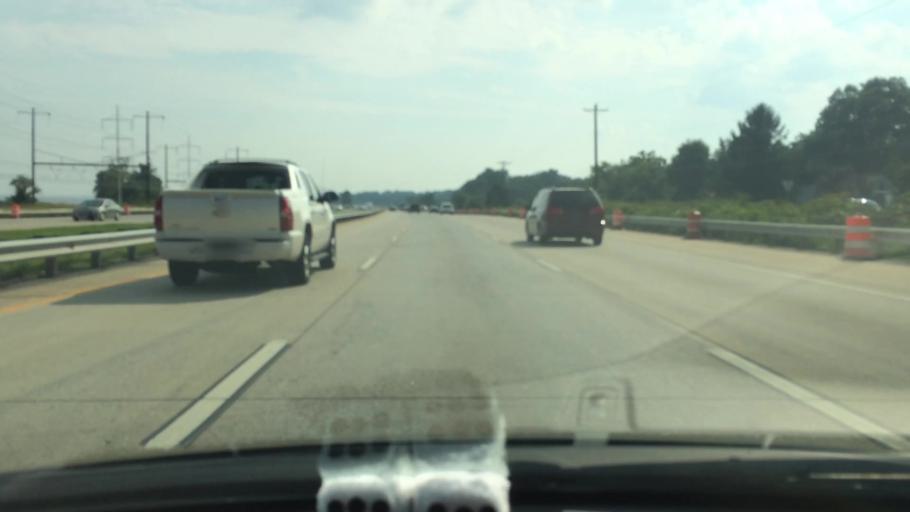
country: US
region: Delaware
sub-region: New Castle County
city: Claymont
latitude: 39.7871
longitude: -75.4697
